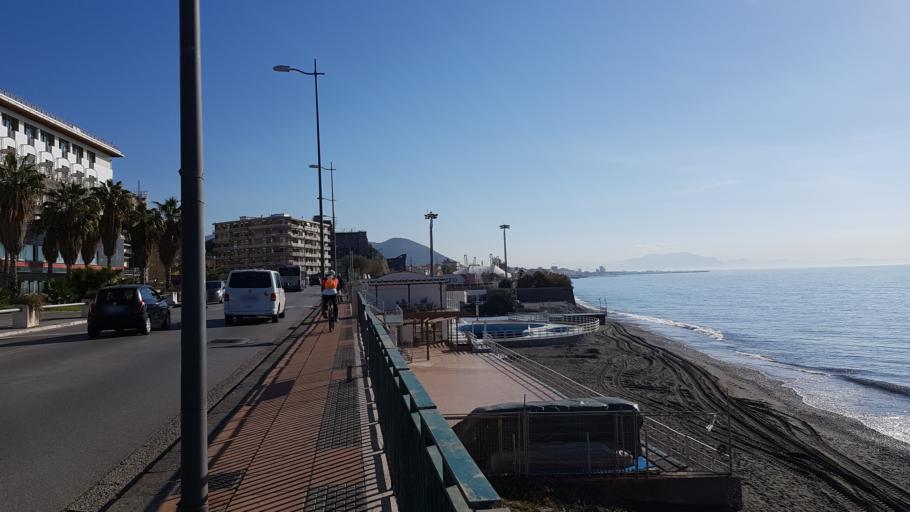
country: IT
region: Campania
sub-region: Provincia di Salerno
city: Salerno
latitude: 40.6721
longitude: 14.7754
